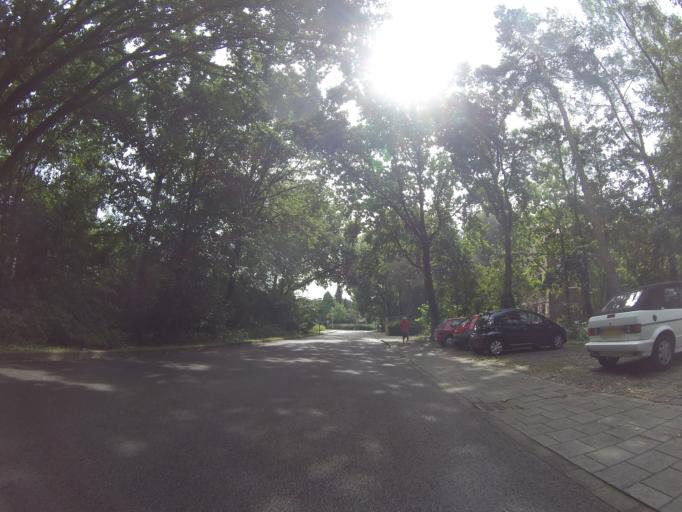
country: NL
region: Utrecht
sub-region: Gemeente Amersfoort
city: Amersfoort
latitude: 52.1360
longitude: 5.3677
